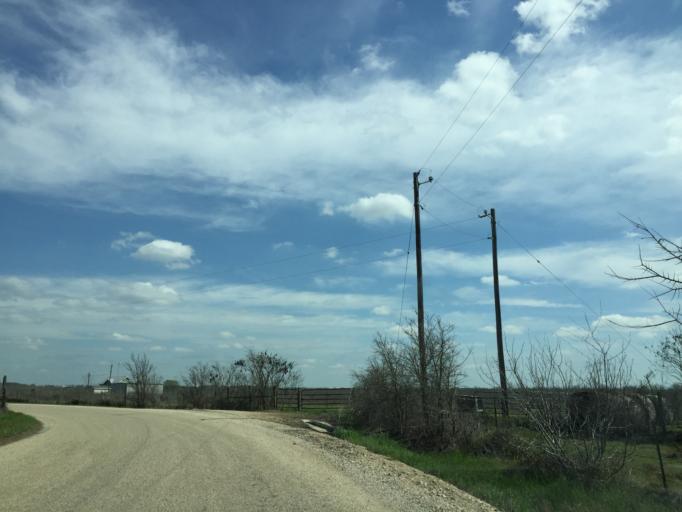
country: US
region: Texas
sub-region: Milam County
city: Thorndale
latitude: 30.5581
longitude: -97.2076
